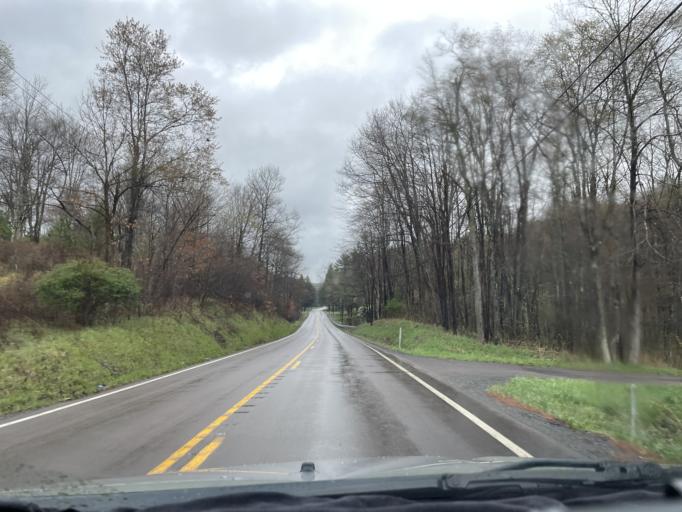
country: US
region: Maryland
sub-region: Garrett County
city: Mountain Lake Park
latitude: 39.4564
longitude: -79.2471
